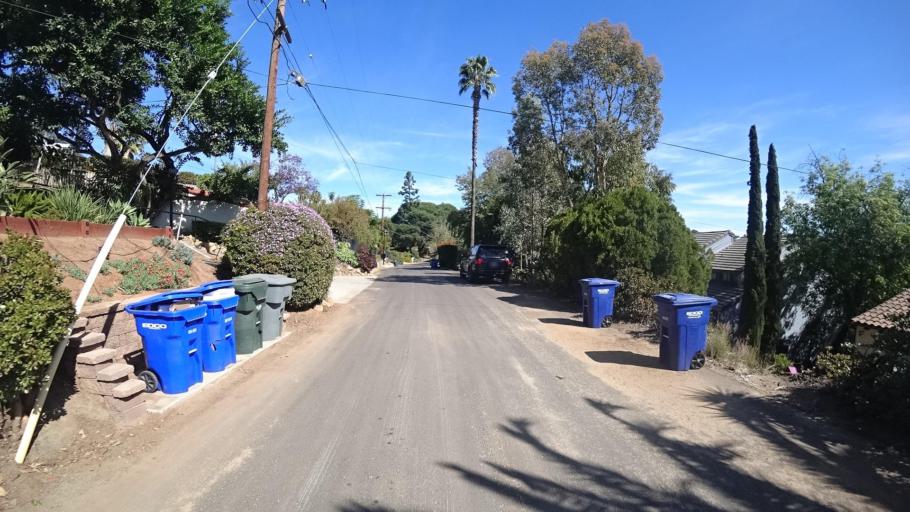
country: US
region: California
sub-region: San Diego County
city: Casa de Oro-Mount Helix
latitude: 32.7598
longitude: -116.9661
